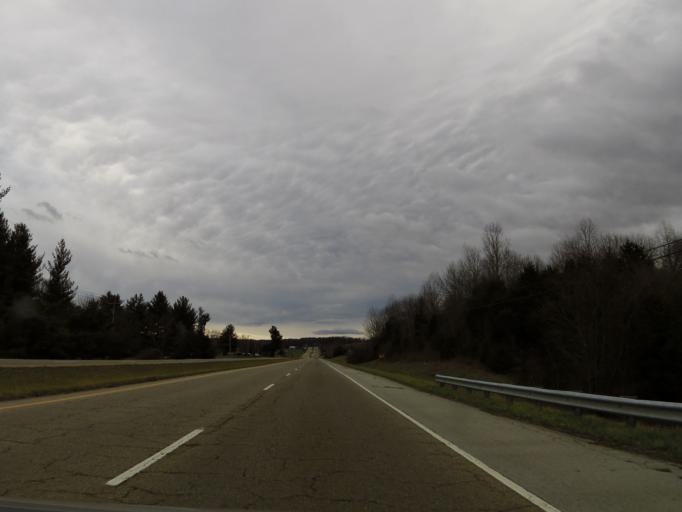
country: US
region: Tennessee
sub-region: Washington County
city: Jonesborough
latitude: 36.2573
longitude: -82.5770
